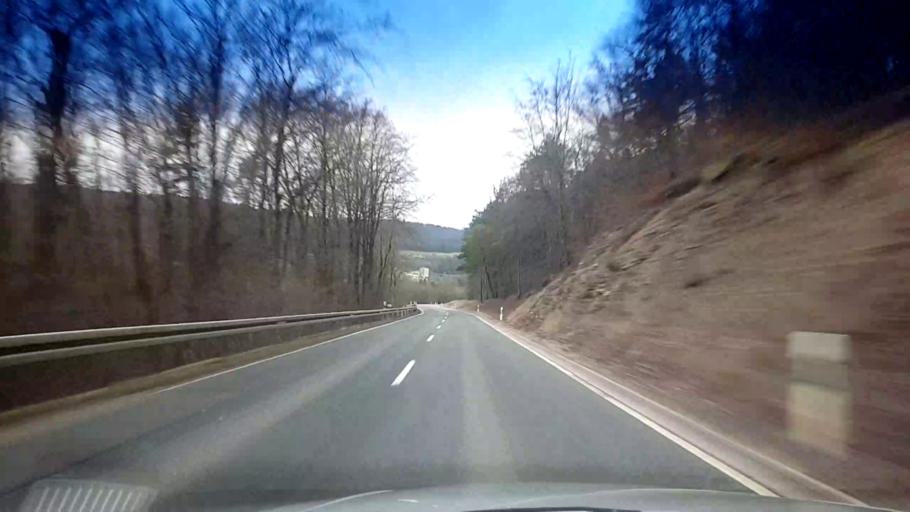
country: DE
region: Bavaria
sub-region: Upper Franconia
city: Wattendorf
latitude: 50.0514
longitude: 11.0873
